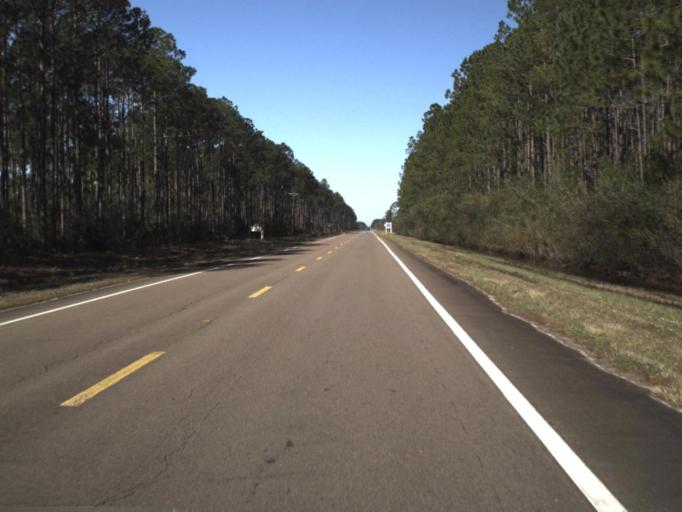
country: US
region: Florida
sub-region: Bay County
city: Callaway
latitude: 30.1381
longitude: -85.3868
